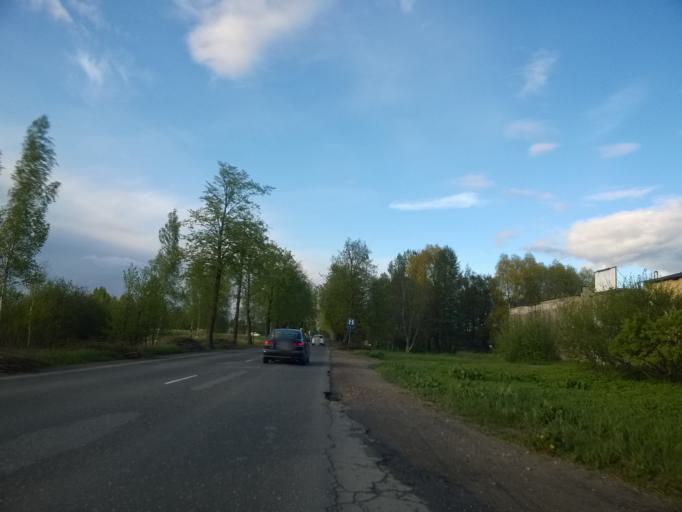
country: LV
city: Tireli
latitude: 56.9404
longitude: 23.6027
